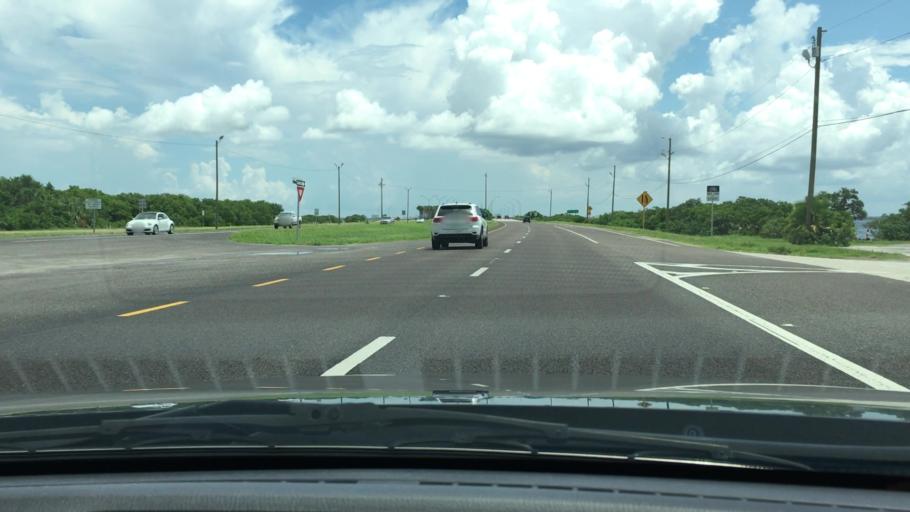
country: US
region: Florida
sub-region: Pinellas County
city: Gandy
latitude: 27.8775
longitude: -82.5886
